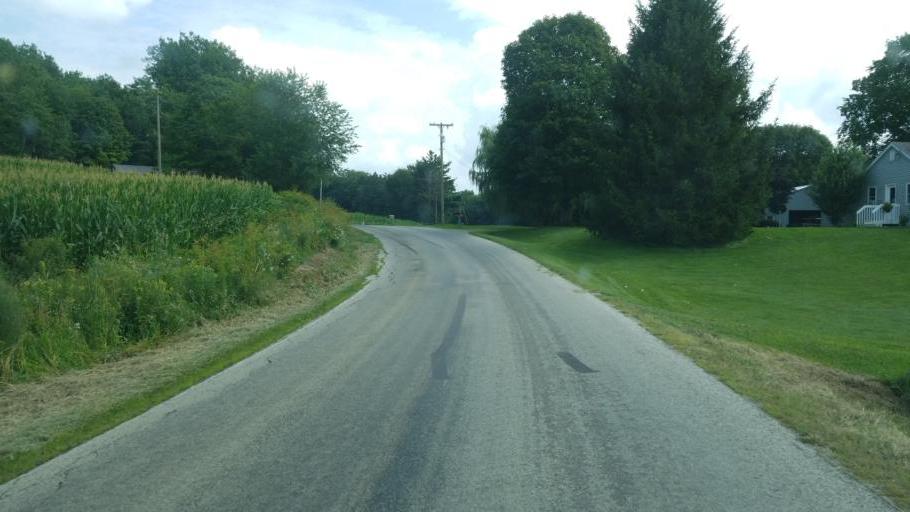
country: US
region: Ohio
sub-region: Sandusky County
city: Bellville
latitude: 40.5715
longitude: -82.4050
